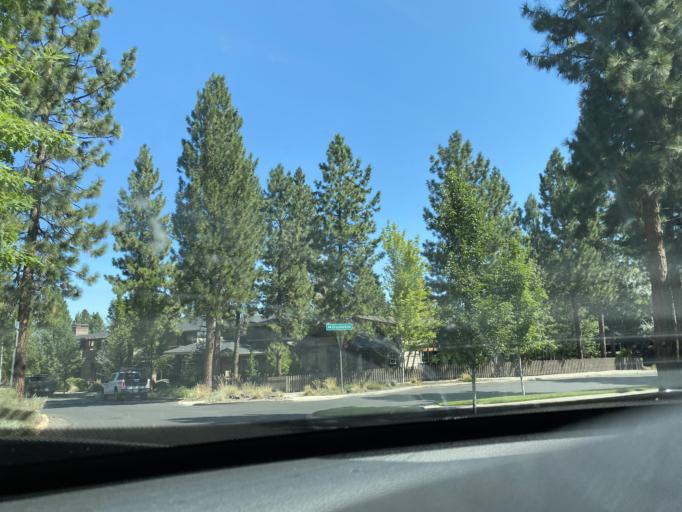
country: US
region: Oregon
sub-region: Deschutes County
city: Bend
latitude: 44.0586
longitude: -121.3501
